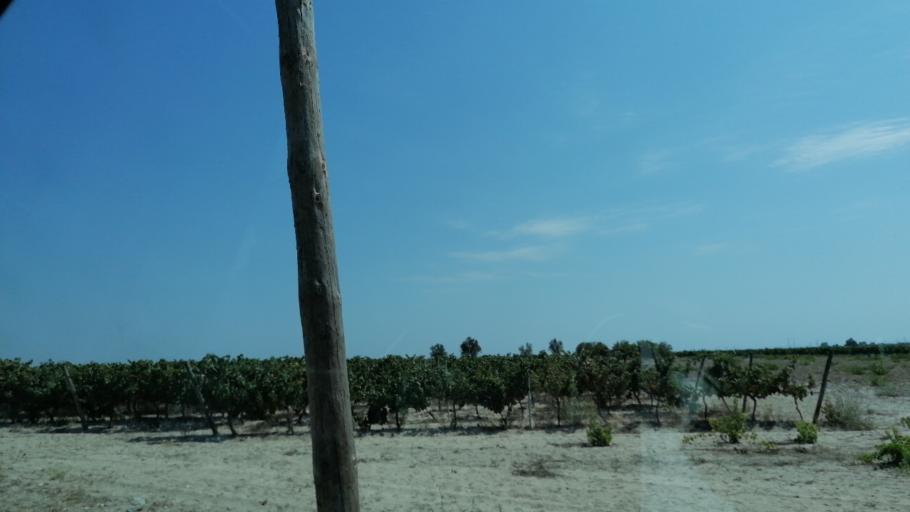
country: PT
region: Setubal
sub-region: Palmela
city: Palmela
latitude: 38.6059
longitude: -8.8406
